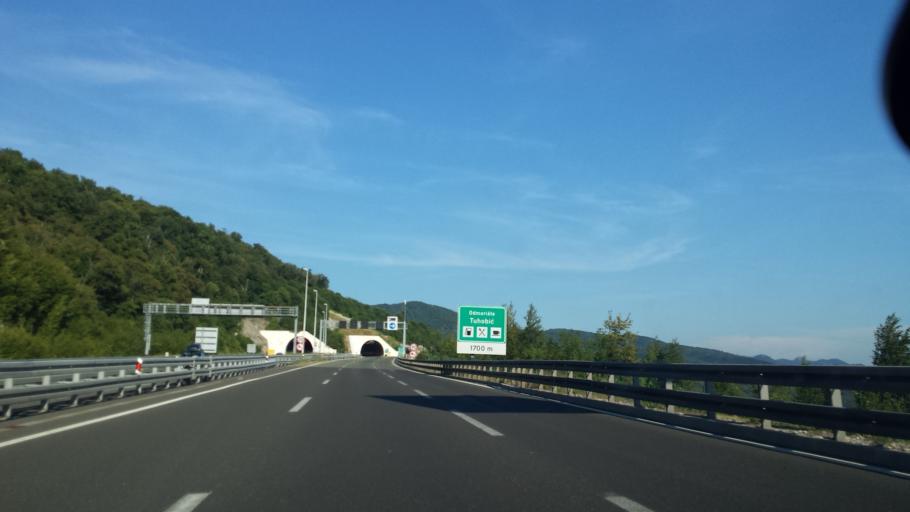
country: HR
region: Primorsko-Goranska
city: Hreljin
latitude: 45.3305
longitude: 14.6016
